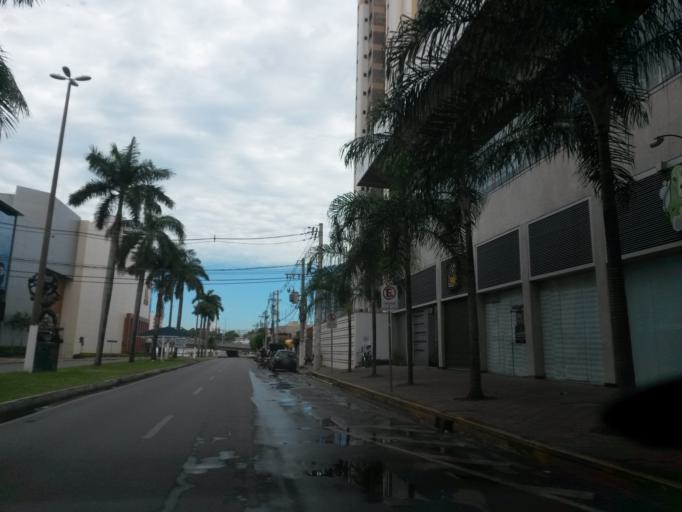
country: BR
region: Mato Grosso
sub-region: Cuiaba
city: Cuiaba
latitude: -15.6116
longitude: -56.0735
